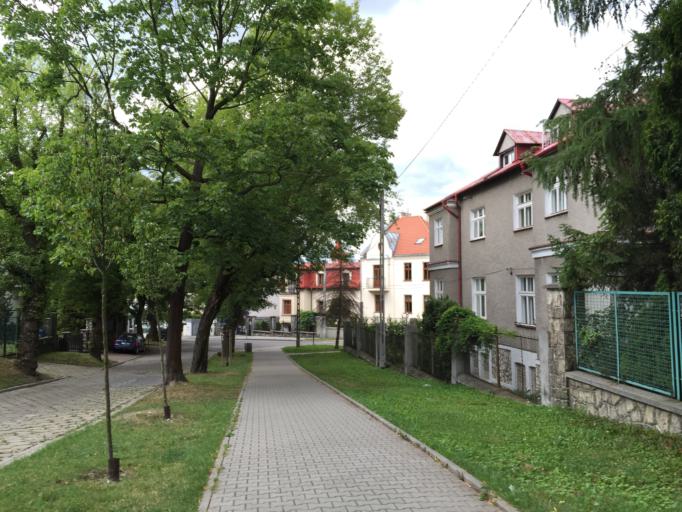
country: PL
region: Lesser Poland Voivodeship
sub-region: Krakow
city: Krakow
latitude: 50.0420
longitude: 19.9539
